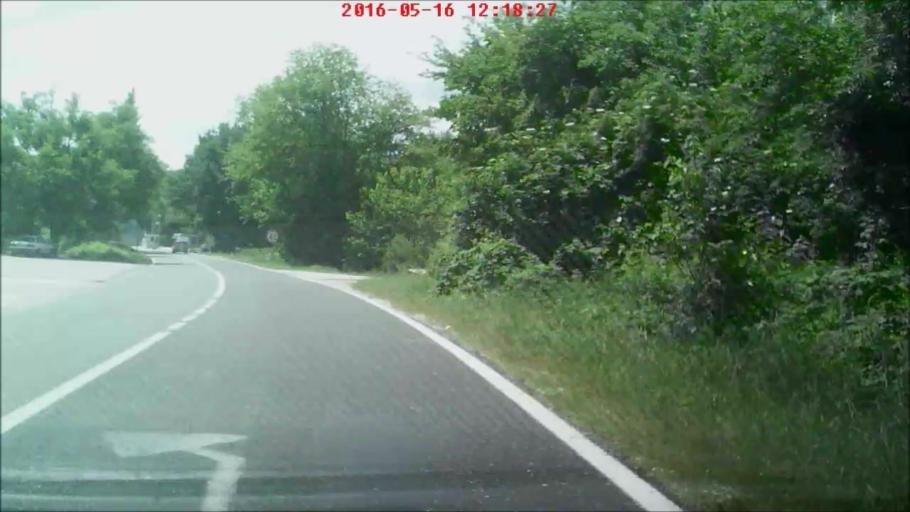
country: HR
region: Dubrovacko-Neretvanska
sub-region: Grad Dubrovnik
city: Metkovic
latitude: 43.0534
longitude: 17.6787
